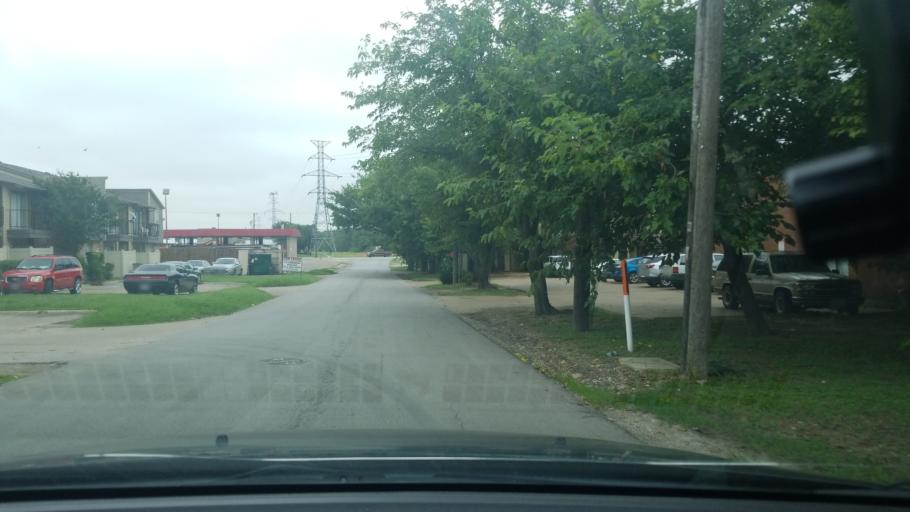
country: US
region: Texas
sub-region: Dallas County
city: Balch Springs
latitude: 32.7685
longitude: -96.6844
